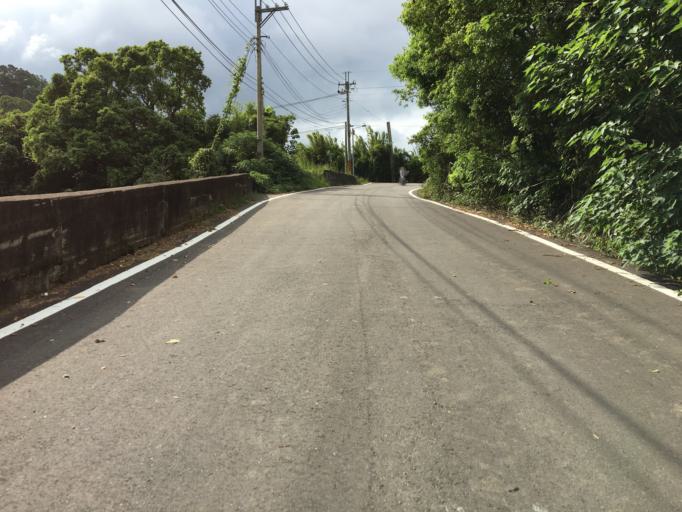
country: TW
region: Taiwan
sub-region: Hsinchu
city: Hsinchu
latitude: 24.7040
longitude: 120.9554
